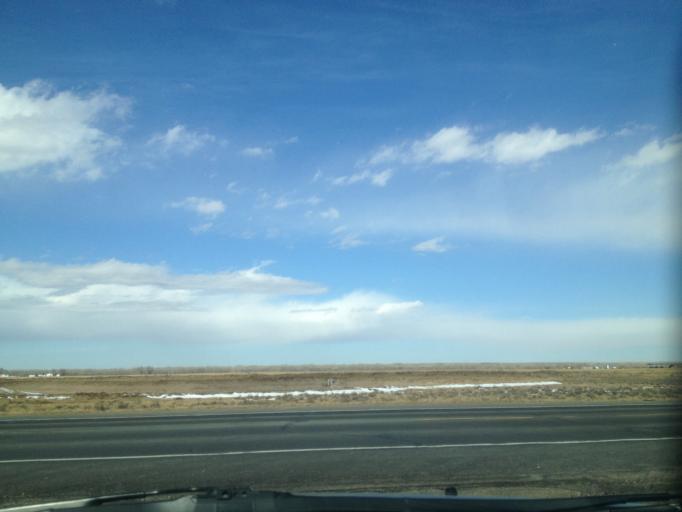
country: US
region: Colorado
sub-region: Weld County
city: Kersey
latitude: 40.2911
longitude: -104.2626
